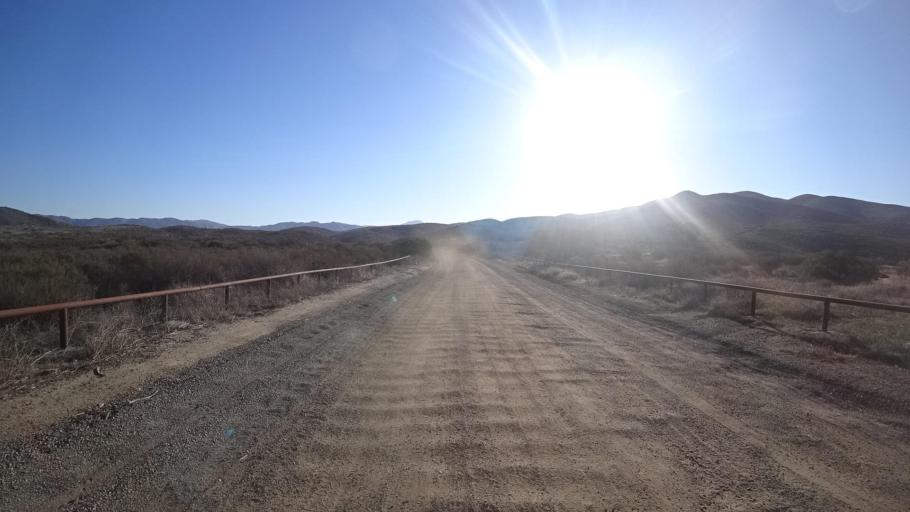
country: US
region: California
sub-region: San Diego County
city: Jamul
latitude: 32.6926
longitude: -116.9061
